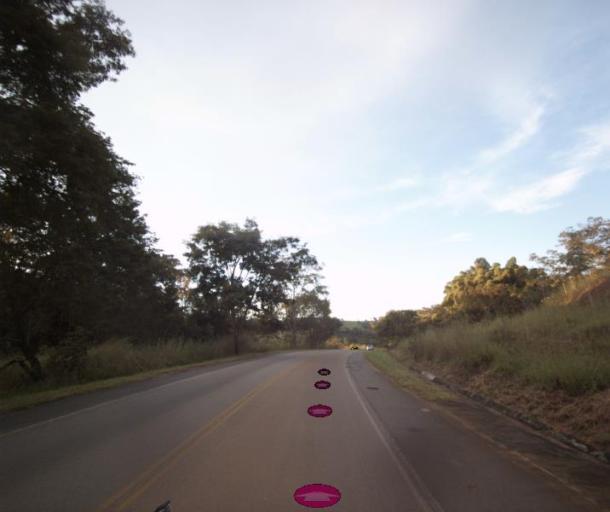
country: BR
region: Goias
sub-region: Abadiania
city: Abadiania
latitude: -16.1281
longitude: -48.8950
